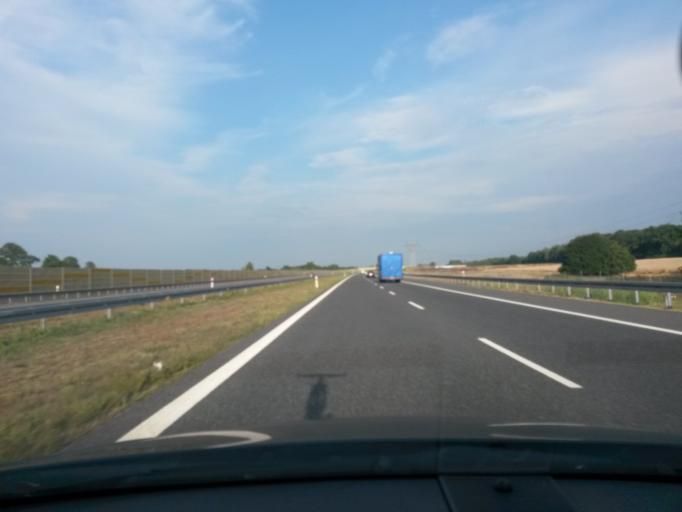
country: PL
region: Lodz Voivodeship
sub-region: Powiat zgierski
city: Ozorkow
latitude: 51.9282
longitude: 19.3098
